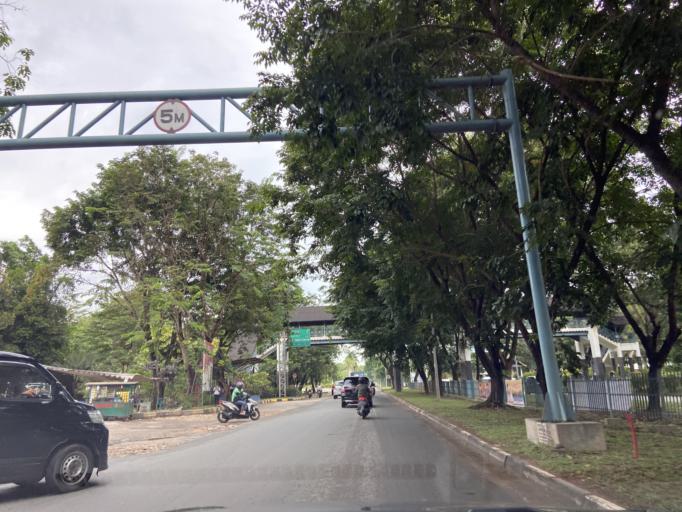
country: SG
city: Singapore
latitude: 1.1071
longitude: 103.9529
